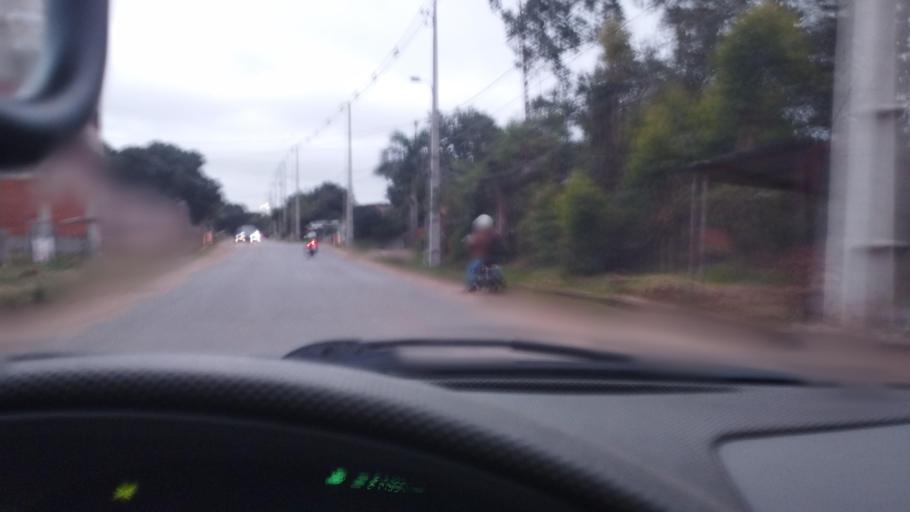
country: PY
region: Central
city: Fernando de la Mora
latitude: -25.2898
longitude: -57.5128
